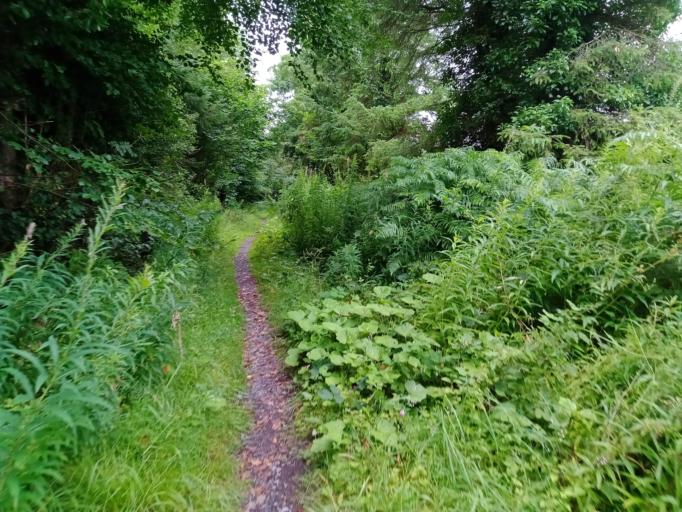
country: IE
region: Leinster
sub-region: Kilkenny
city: Ballyragget
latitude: 52.8282
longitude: -7.3984
